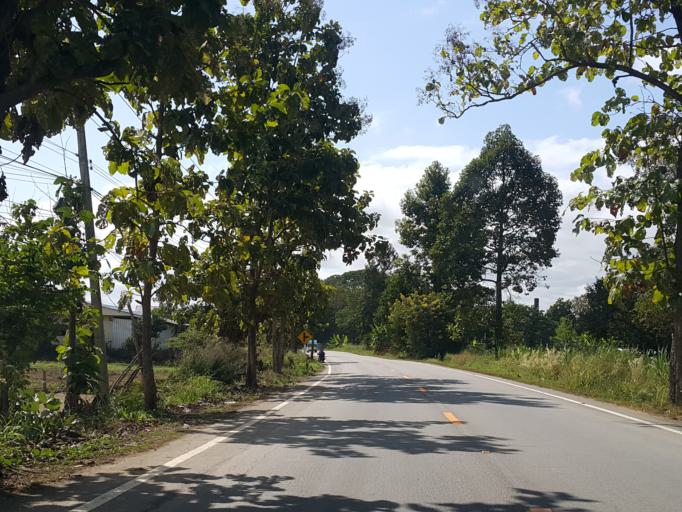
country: TH
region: Chiang Mai
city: San Kamphaeng
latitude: 18.7094
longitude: 99.1676
